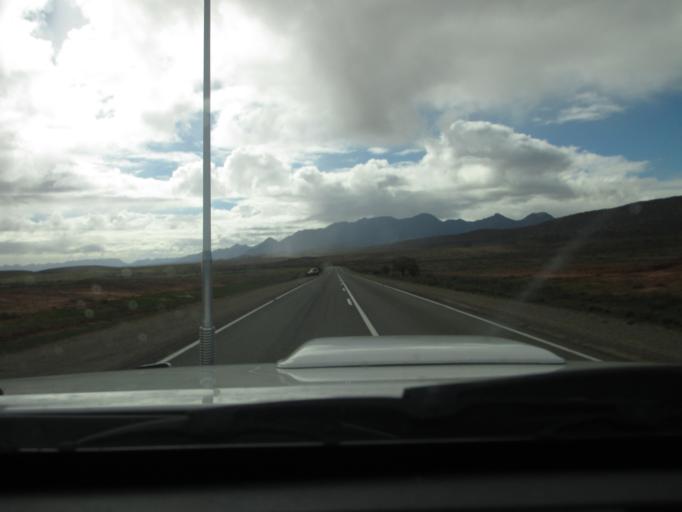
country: AU
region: South Australia
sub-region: Flinders Ranges
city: Quorn
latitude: -31.5956
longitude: 138.4079
